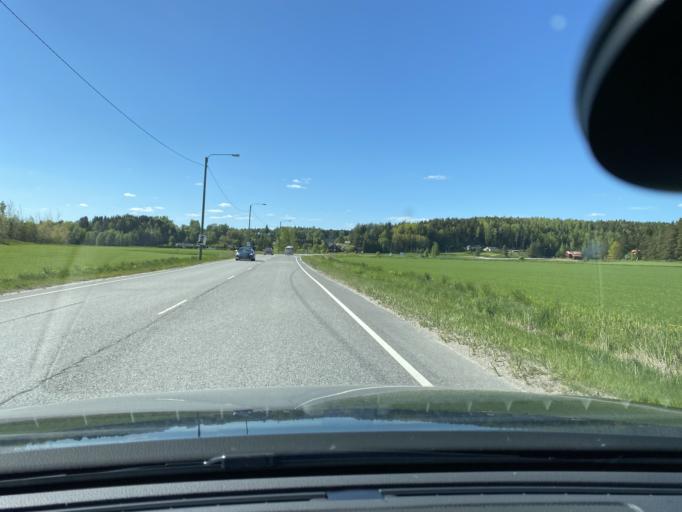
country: FI
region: Varsinais-Suomi
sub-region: Turku
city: Sauvo
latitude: 60.3516
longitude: 22.6744
